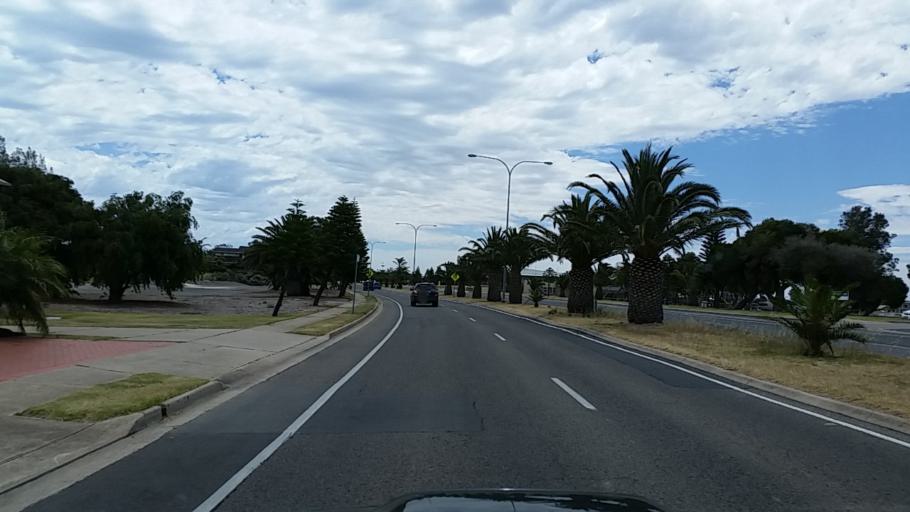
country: AU
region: South Australia
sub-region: Charles Sturt
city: West Lakes Shore
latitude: -34.8770
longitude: 138.4847
